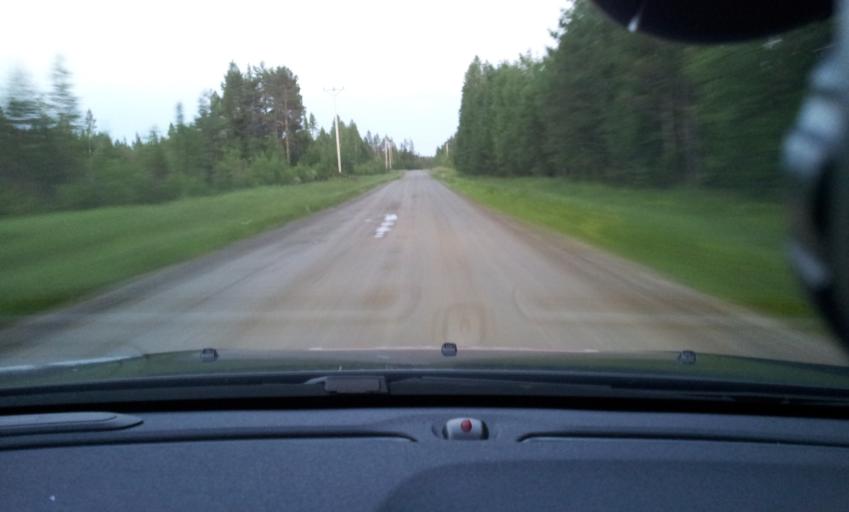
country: SE
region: Vaesternorrland
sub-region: Ange Kommun
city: Fransta
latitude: 62.8250
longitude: 16.0026
